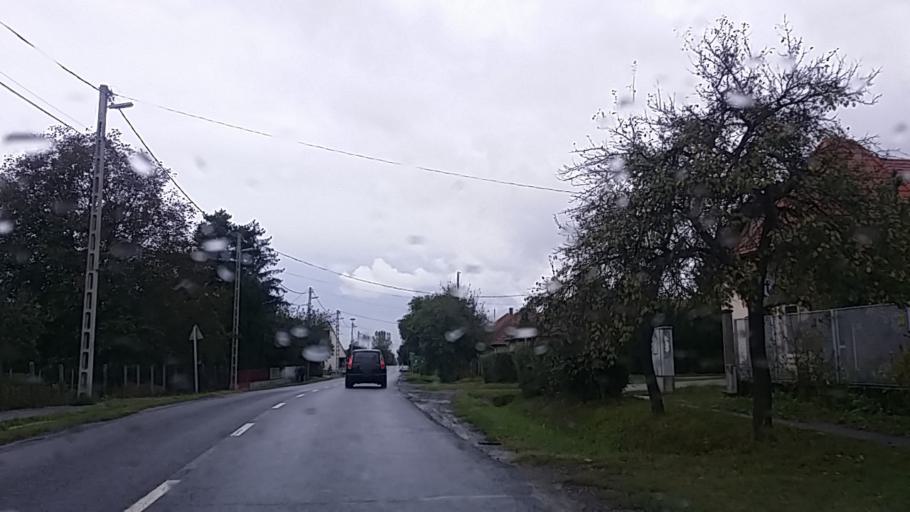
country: HU
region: Komarom-Esztergom
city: Esztergom
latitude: 47.8865
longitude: 18.7760
